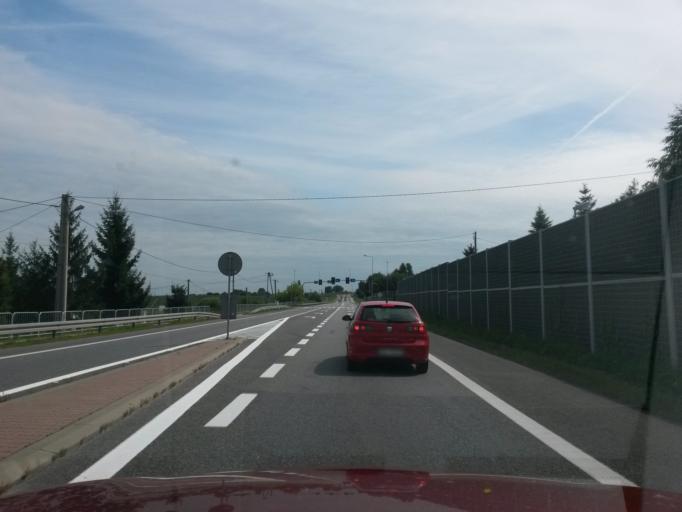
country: PL
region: Lesser Poland Voivodeship
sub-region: Powiat brzeski
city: Jasien
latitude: 49.9731
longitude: 20.5725
